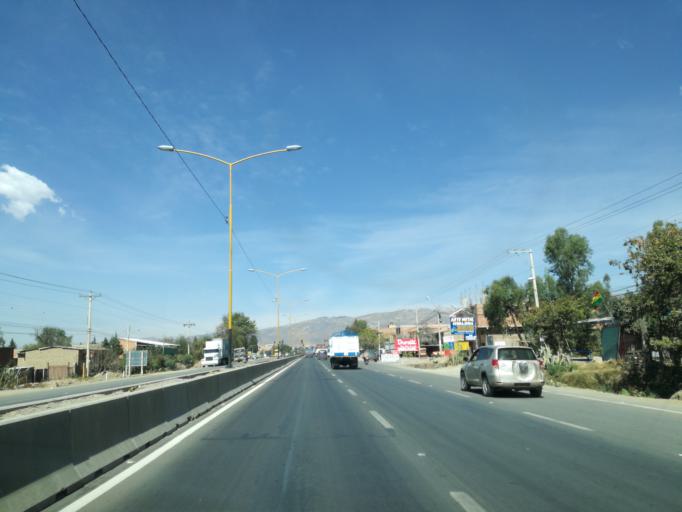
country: BO
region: Cochabamba
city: Sipe Sipe
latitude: -17.4062
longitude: -66.3307
